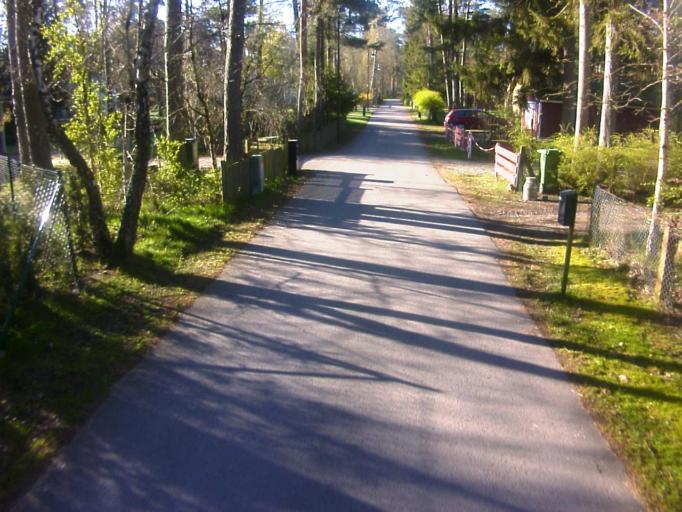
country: SE
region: Skane
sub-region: Kavlinge Kommun
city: Hofterup
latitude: 55.8161
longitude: 12.9719
